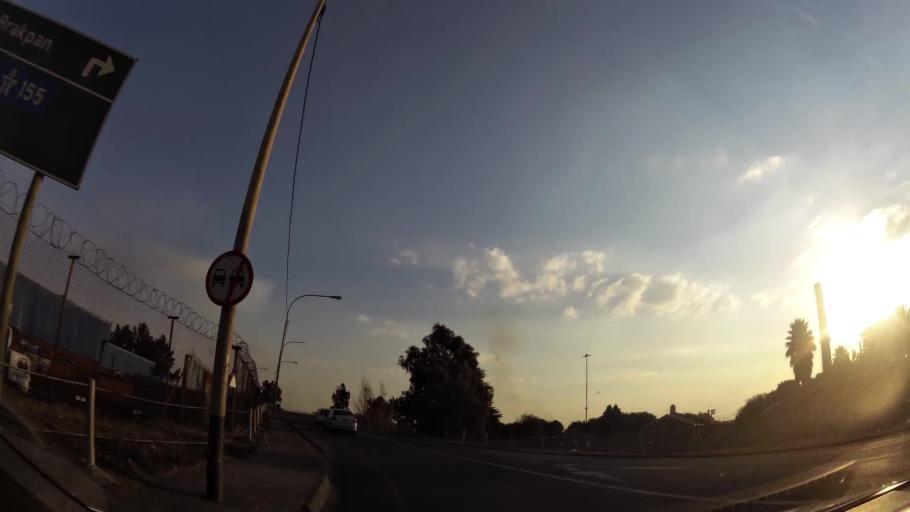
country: ZA
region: Gauteng
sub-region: Ekurhuleni Metropolitan Municipality
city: Springs
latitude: -26.2639
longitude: 28.4185
